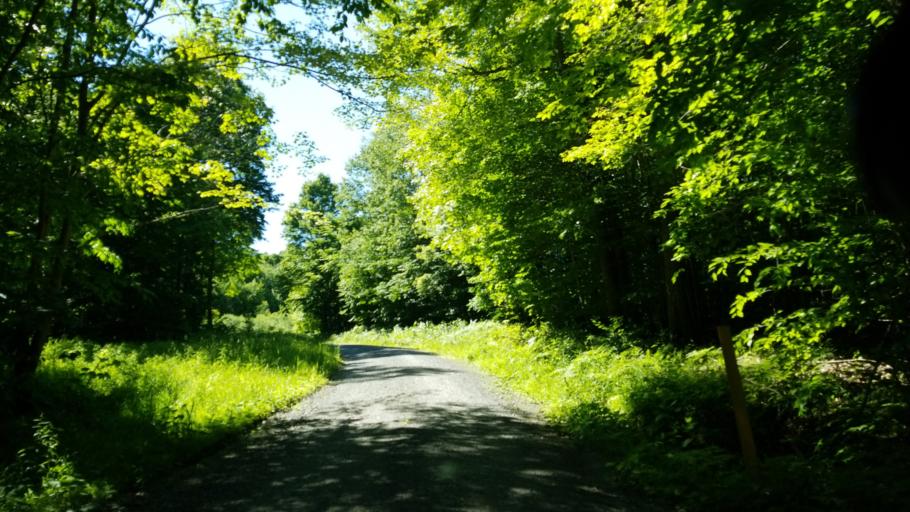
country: US
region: Pennsylvania
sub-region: Clearfield County
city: Clearfield
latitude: 41.2120
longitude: -78.3918
